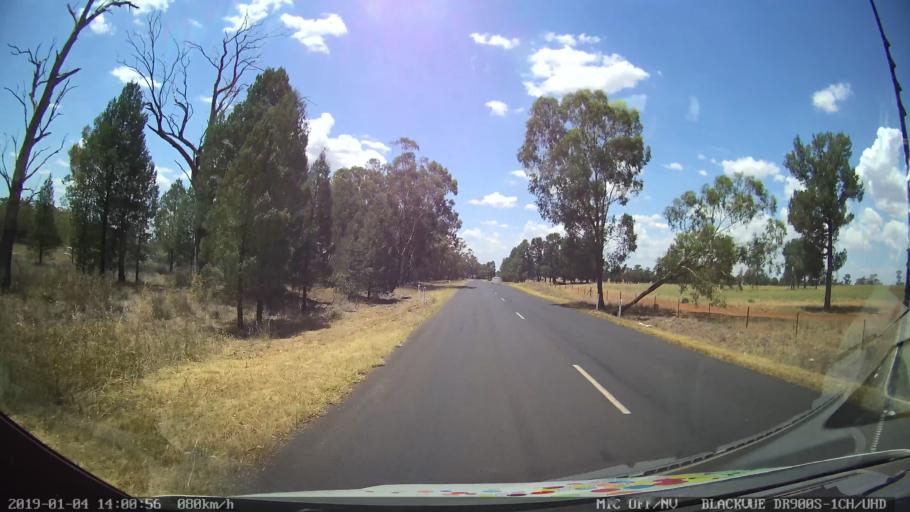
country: AU
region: New South Wales
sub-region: Dubbo Municipality
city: Dubbo
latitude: -32.3020
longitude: 148.5967
